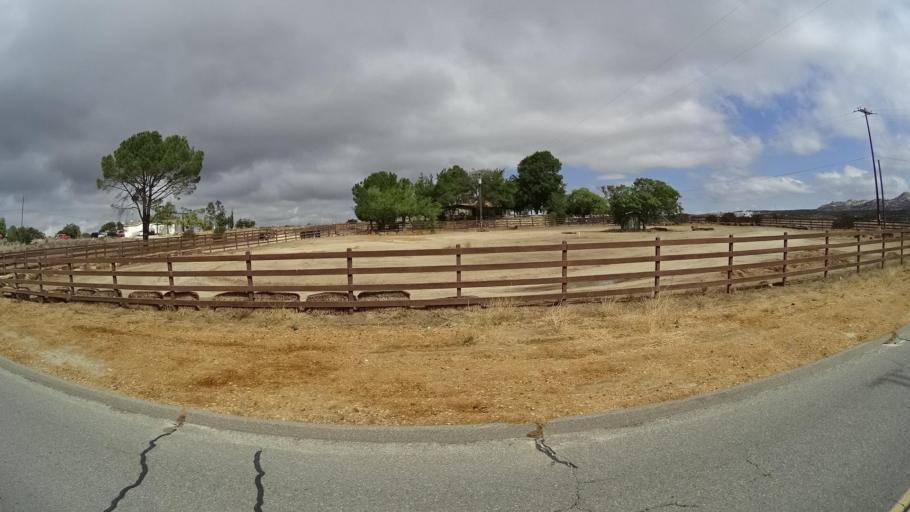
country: US
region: California
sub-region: San Diego County
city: Campo
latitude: 32.6096
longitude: -116.3246
